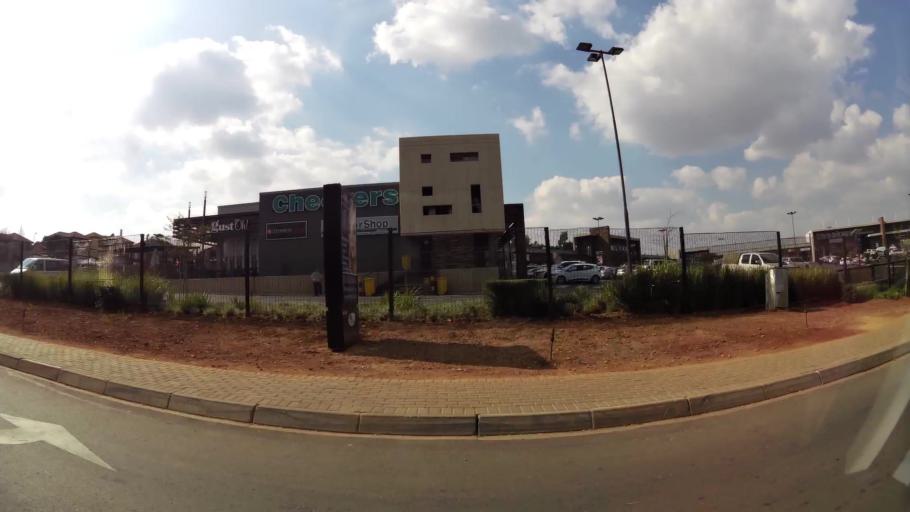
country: ZA
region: Gauteng
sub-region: City of Tshwane Metropolitan Municipality
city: Pretoria
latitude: -25.7988
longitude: 28.3322
